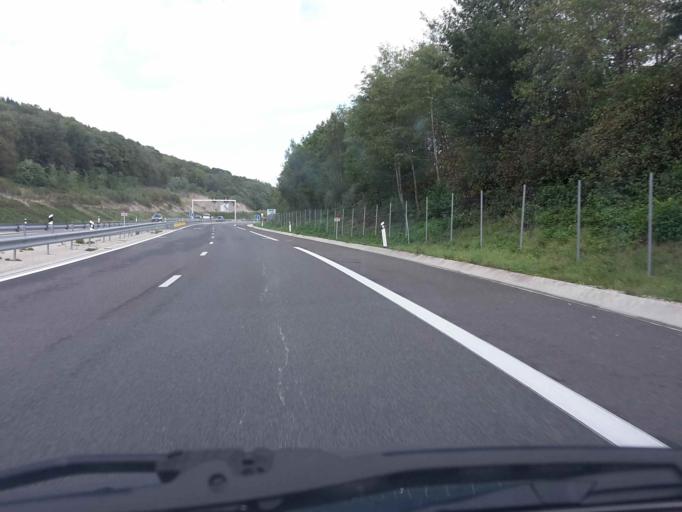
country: FR
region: Franche-Comte
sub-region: Departement du Doubs
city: Morre
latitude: 47.2134
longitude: 6.0613
